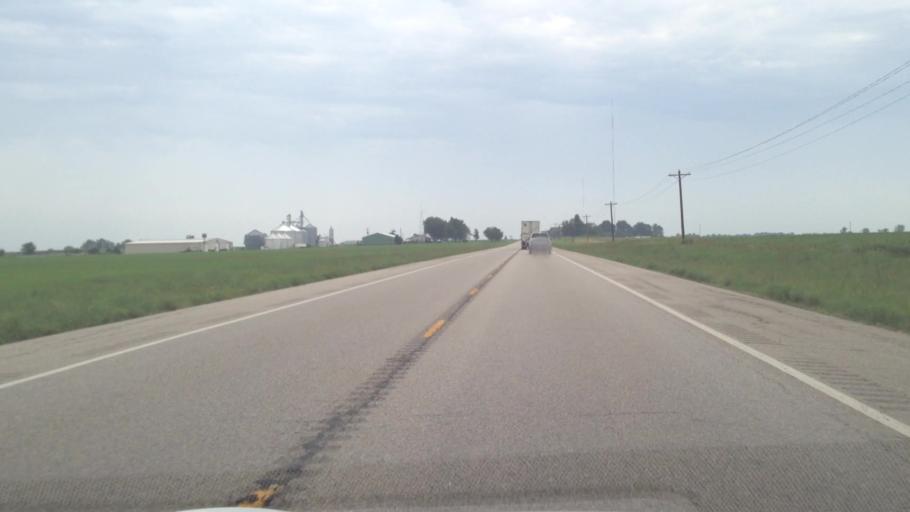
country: US
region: Missouri
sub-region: Jasper County
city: Carl Junction
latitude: 37.2423
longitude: -94.7051
